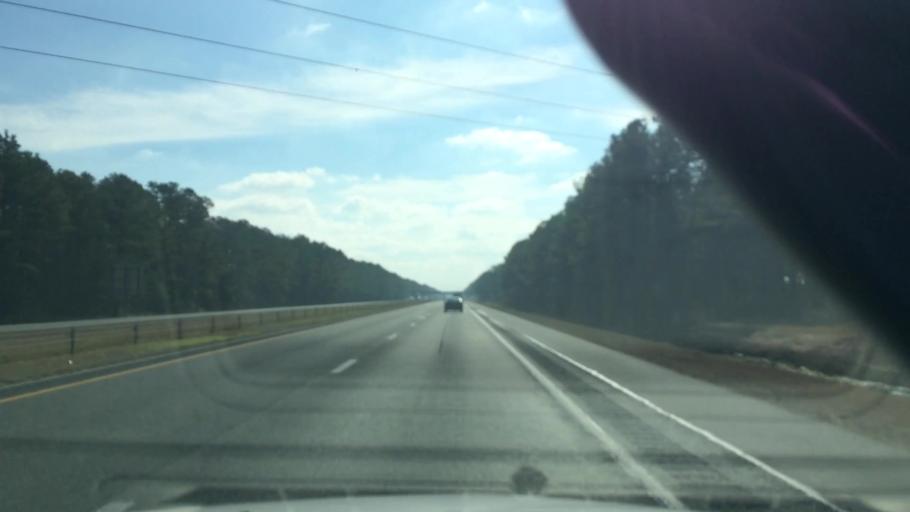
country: US
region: North Carolina
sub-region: Duplin County
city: Wallace
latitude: 34.7393
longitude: -77.9446
